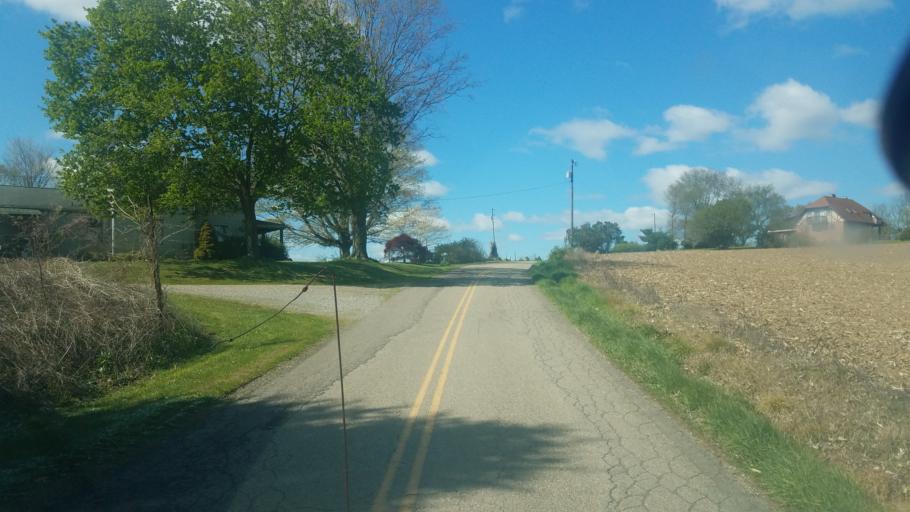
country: US
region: Ohio
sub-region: Knox County
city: Danville
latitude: 40.4348
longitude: -82.3320
